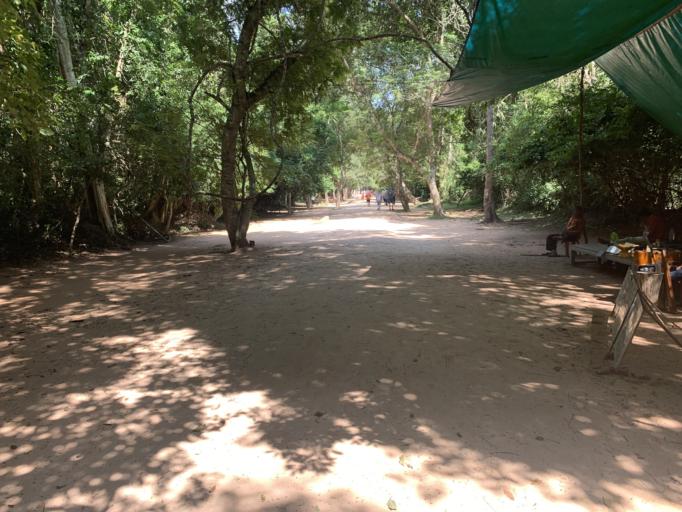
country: KH
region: Siem Reap
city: Siem Reap
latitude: 13.4350
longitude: 103.8929
